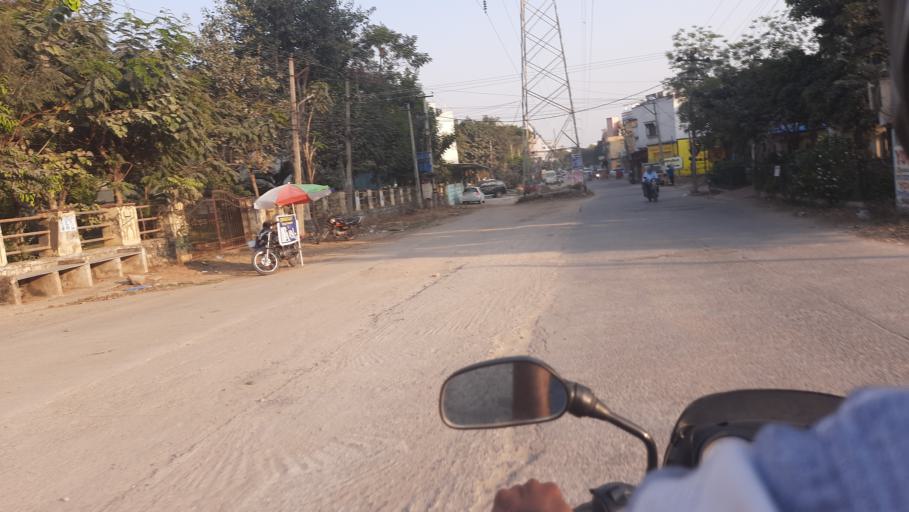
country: IN
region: Telangana
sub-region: Rangareddi
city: Secunderabad
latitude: 17.4986
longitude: 78.5414
